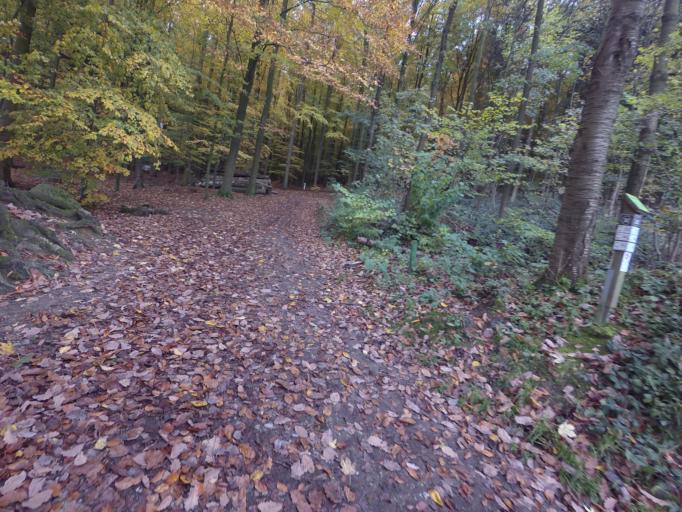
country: NL
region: Limburg
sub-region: Gemeente Vaals
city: Vaals
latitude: 50.7628
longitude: 6.0233
